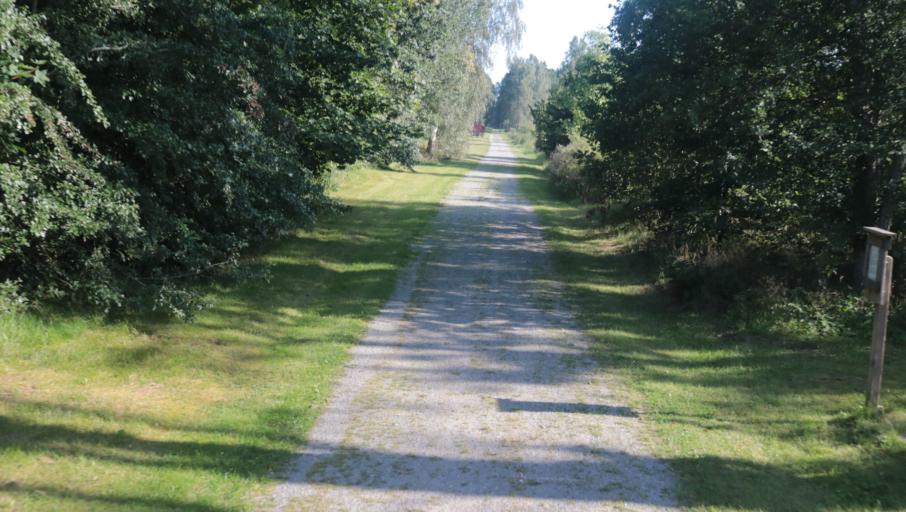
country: SE
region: Blekinge
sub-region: Karlshamns Kommun
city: Svangsta
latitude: 56.3479
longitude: 14.6952
